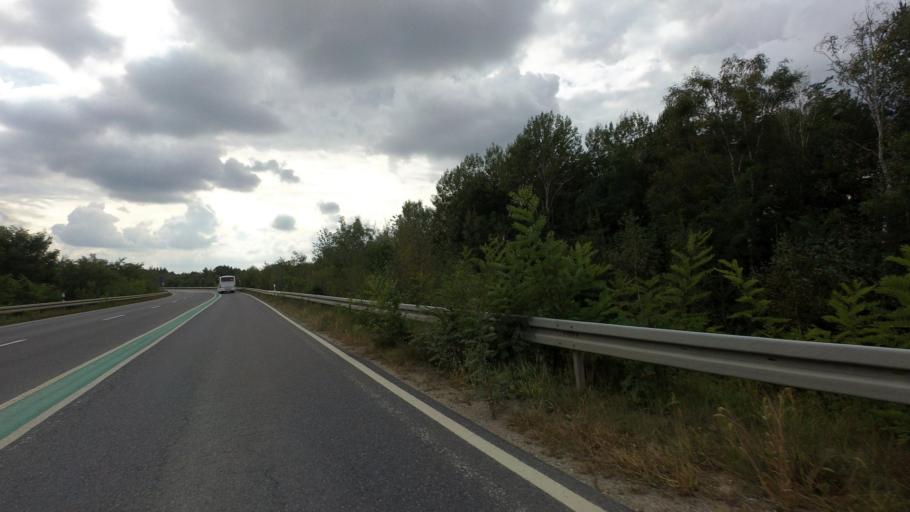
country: DE
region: Brandenburg
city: Senftenberg
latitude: 51.5347
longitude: 14.0248
